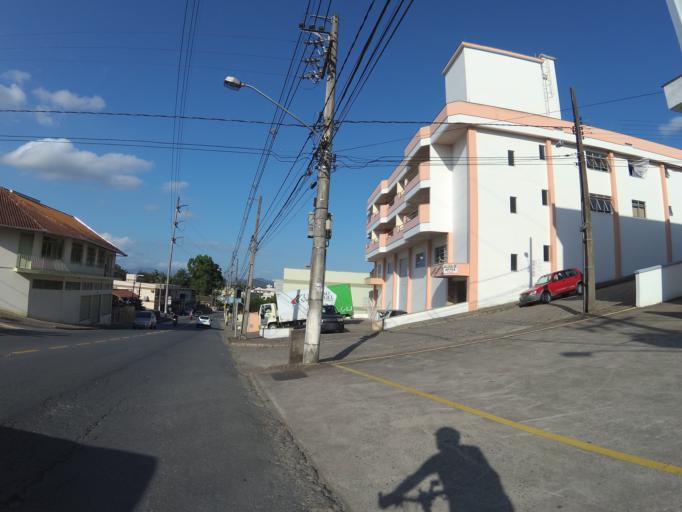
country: BR
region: Santa Catarina
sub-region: Blumenau
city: Blumenau
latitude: -26.9269
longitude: -49.1123
